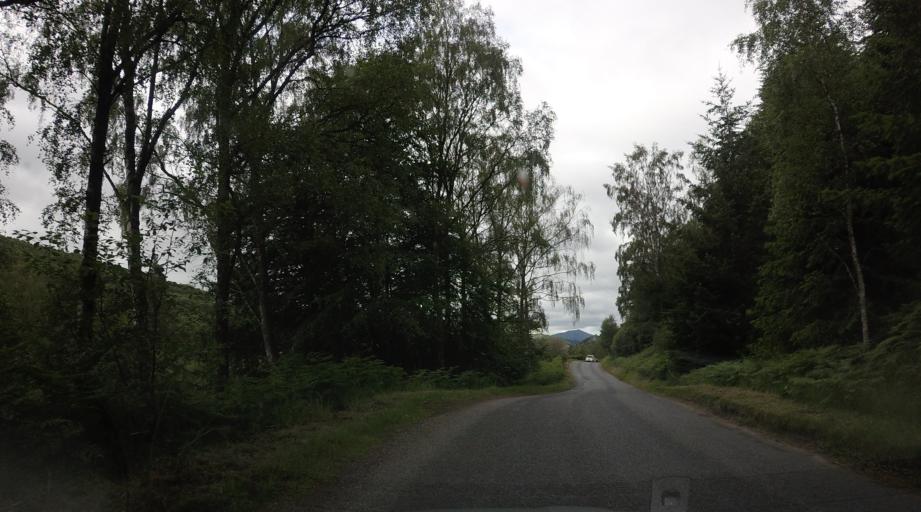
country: GB
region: Scotland
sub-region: Perth and Kinross
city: Pitlochry
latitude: 56.7204
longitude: -3.8296
